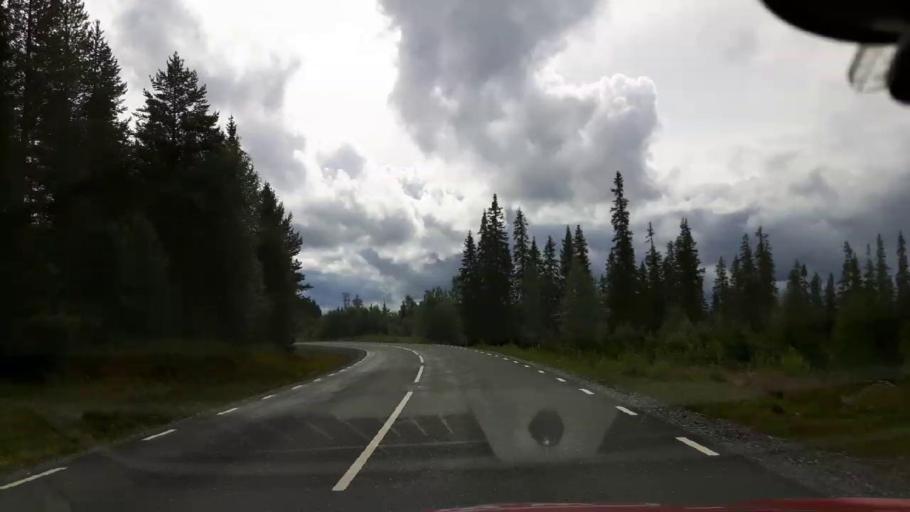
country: NO
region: Nord-Trondelag
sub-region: Lierne
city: Sandvika
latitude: 64.6068
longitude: 14.1197
